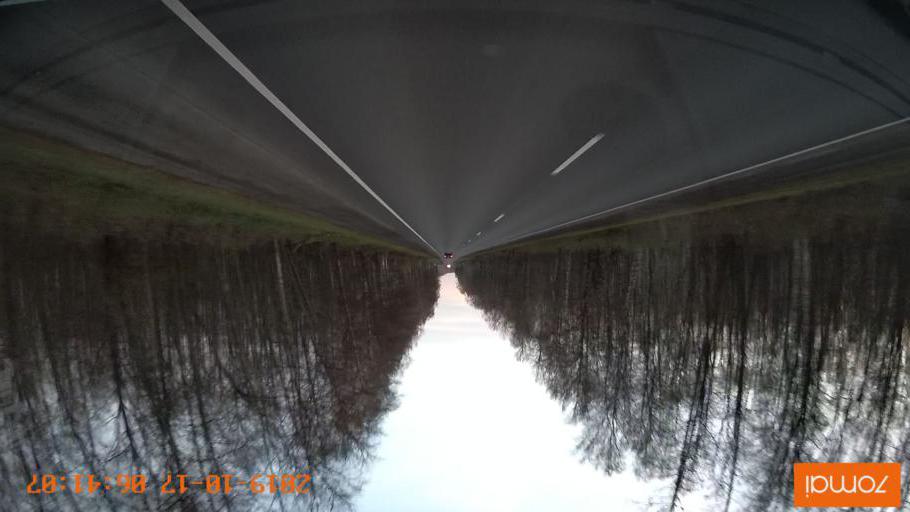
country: RU
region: Ivanovo
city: Nerl'
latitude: 56.6196
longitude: 40.5632
